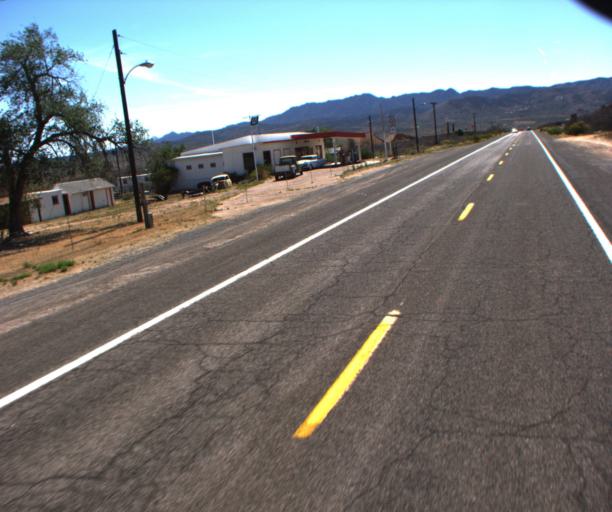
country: US
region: Arizona
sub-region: Mohave County
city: Peach Springs
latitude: 35.3655
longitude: -113.6785
